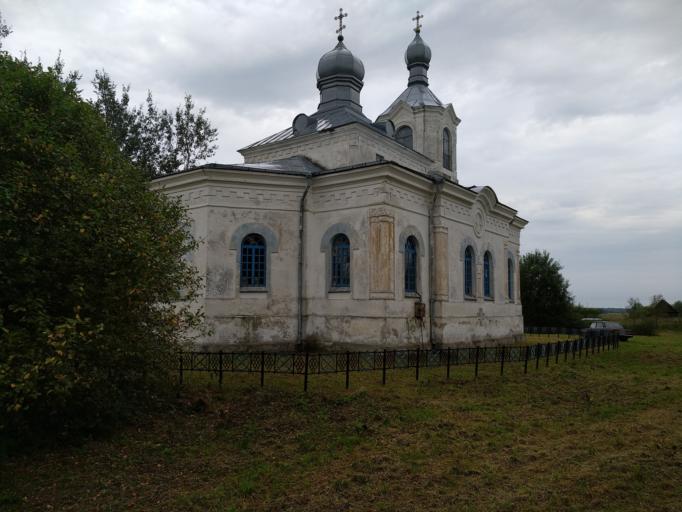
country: BY
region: Vitebsk
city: Sharkawshchyna
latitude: 55.3092
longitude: 27.2594
